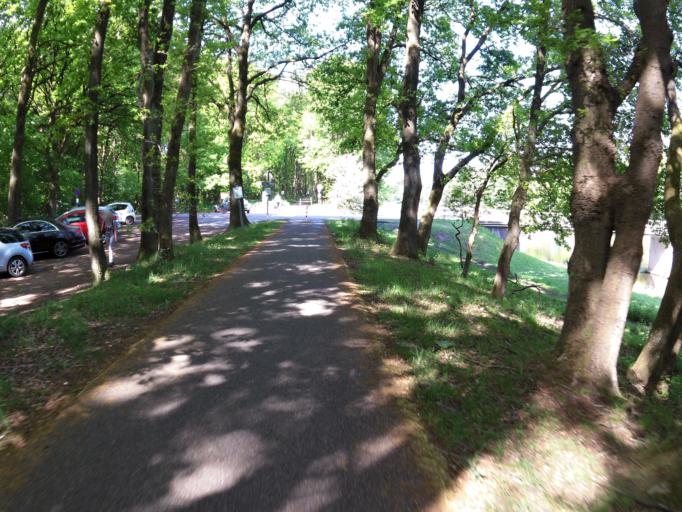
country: NL
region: North Brabant
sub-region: Gemeente Waalwijk
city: Waalwijk
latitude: 51.6690
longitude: 5.1298
